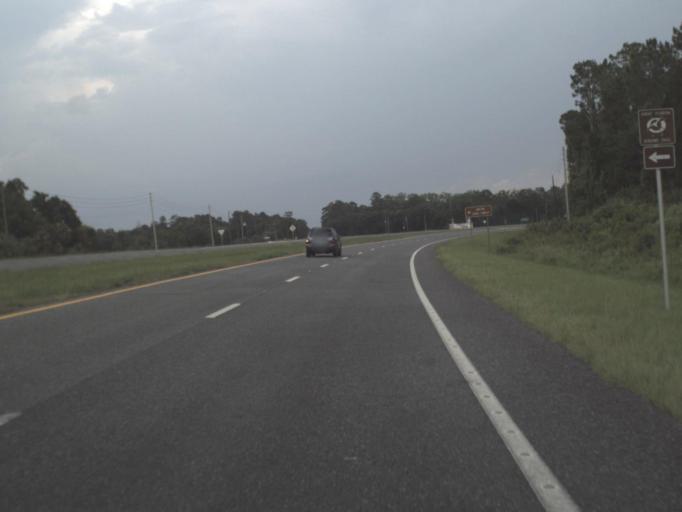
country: US
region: Florida
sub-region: Levy County
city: Inglis
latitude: 29.1671
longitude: -82.6439
